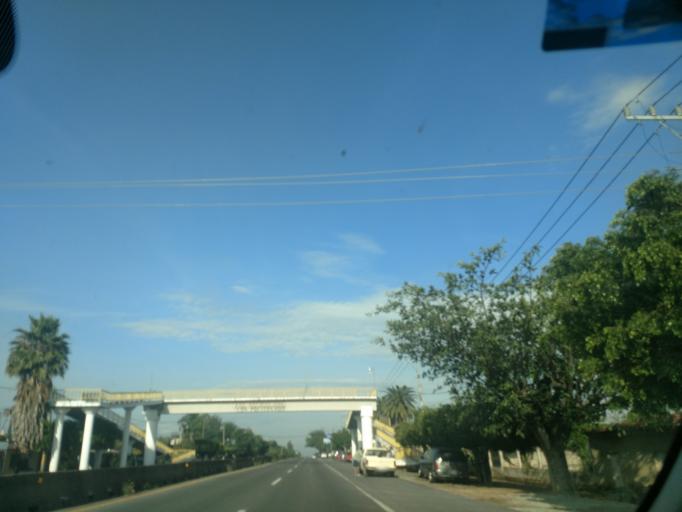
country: MX
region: Jalisco
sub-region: Ameca
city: Los Pocitos
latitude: 20.5370
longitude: -103.9372
